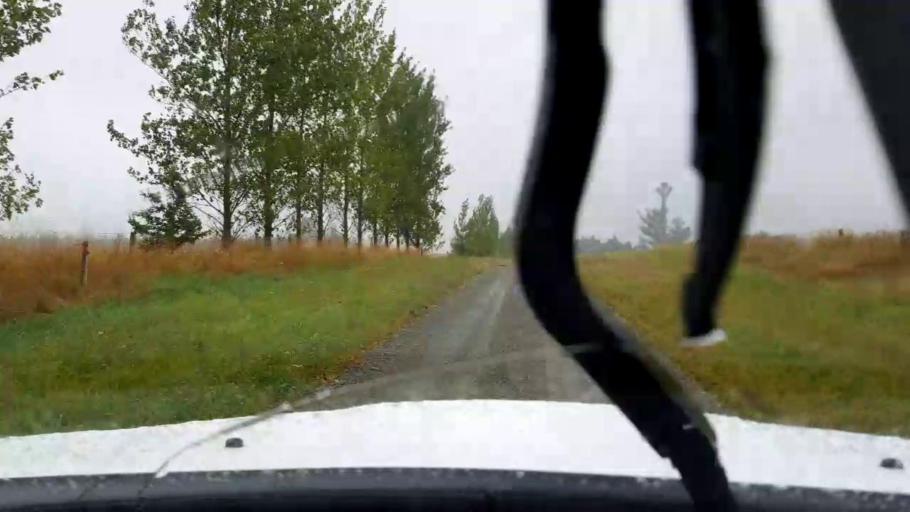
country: NZ
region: Canterbury
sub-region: Timaru District
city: Pleasant Point
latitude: -44.1992
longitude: 171.0905
